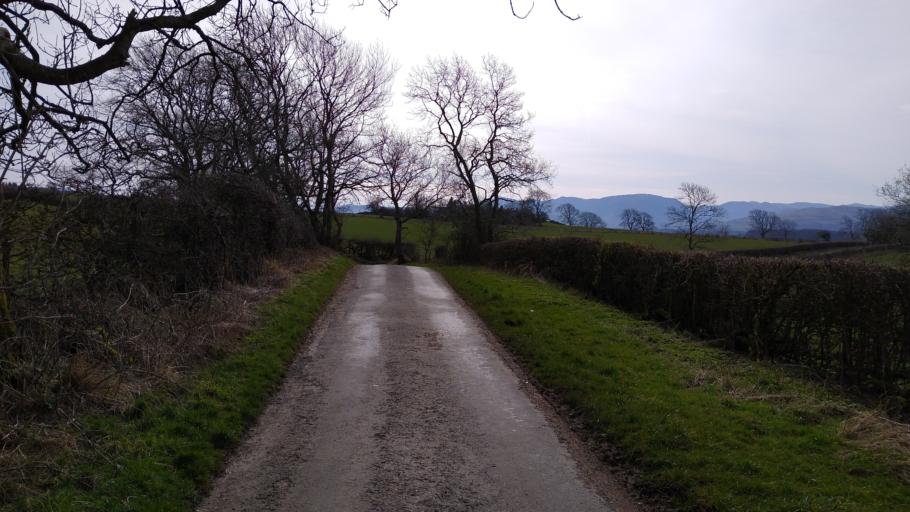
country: GB
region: England
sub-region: Cumbria
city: Cockermouth
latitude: 54.7070
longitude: -3.3699
